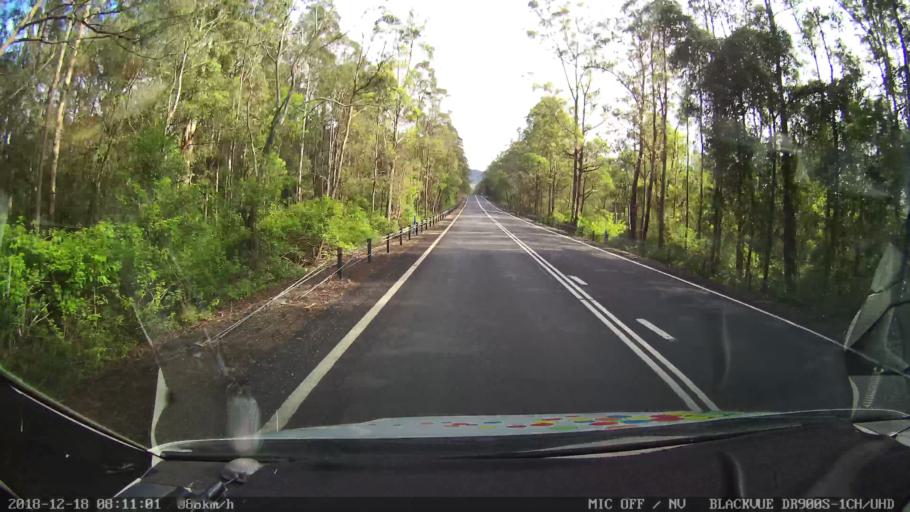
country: AU
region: New South Wales
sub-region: Kyogle
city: Kyogle
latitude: -28.3558
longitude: 152.6668
